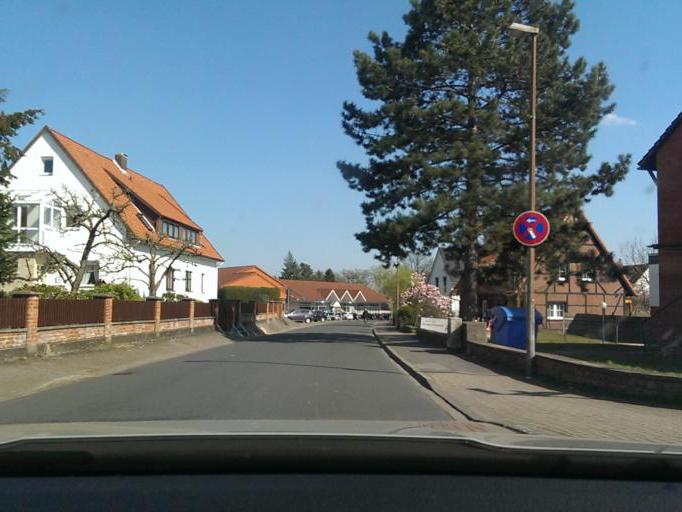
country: DE
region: Lower Saxony
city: Elze
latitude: 52.5479
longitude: 9.7363
